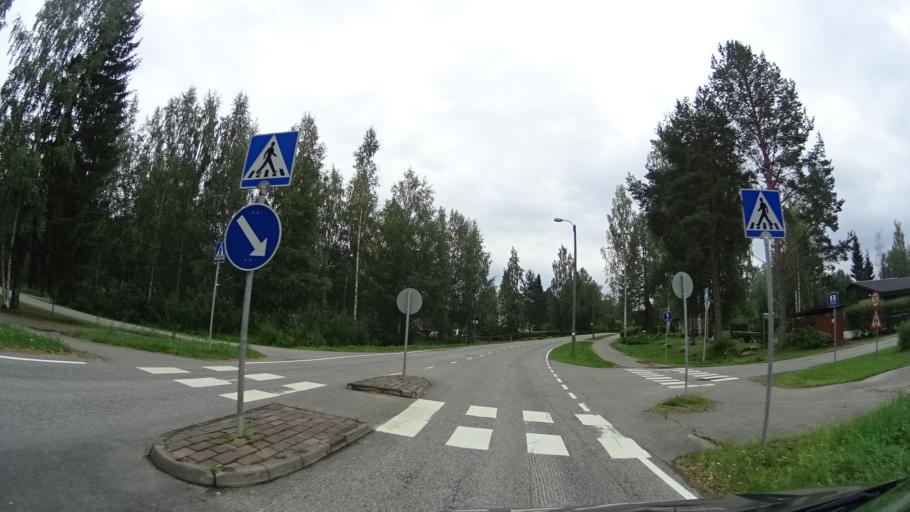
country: FI
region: Southern Savonia
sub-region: Savonlinna
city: Punkaharju
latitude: 61.7524
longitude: 29.3896
